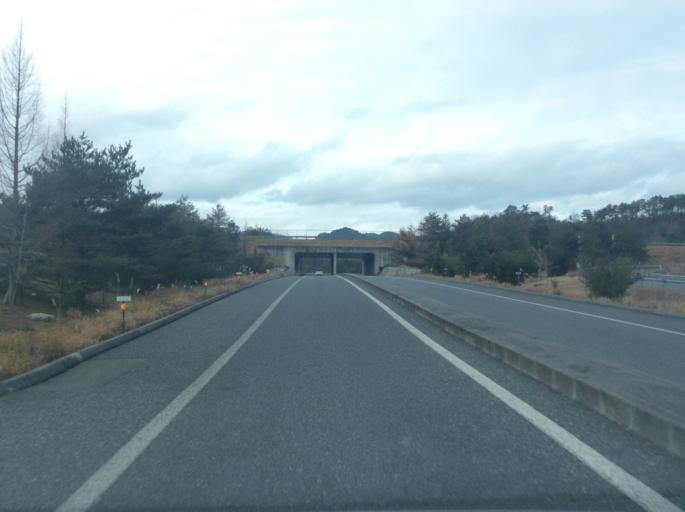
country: JP
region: Fukushima
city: Iwaki
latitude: 37.1259
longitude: 140.9463
